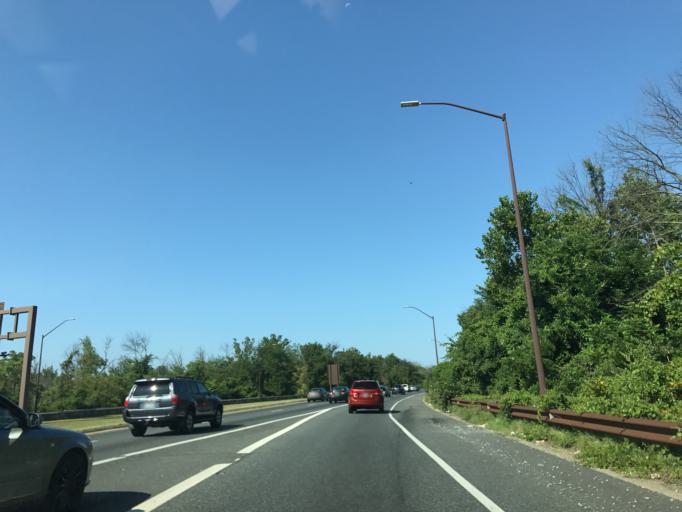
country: US
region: Maryland
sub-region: Prince George's County
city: Colmar Manor
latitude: 38.9193
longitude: -76.9380
